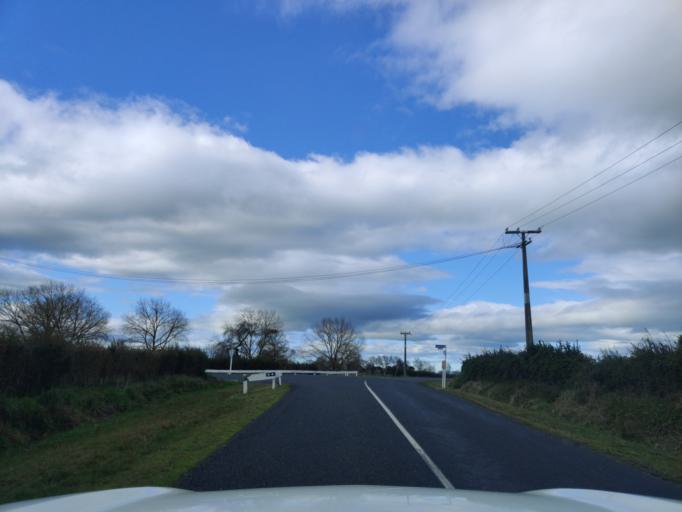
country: NZ
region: Waikato
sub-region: Hauraki District
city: Paeroa
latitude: -37.5943
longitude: 175.5223
